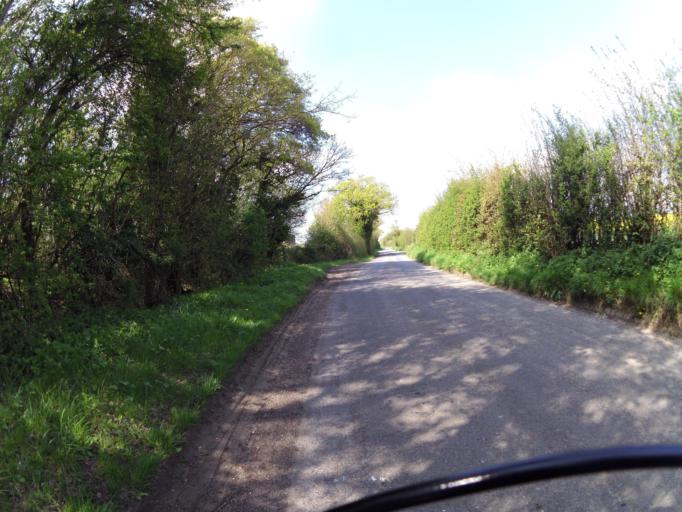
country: GB
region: England
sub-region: Suffolk
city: Bramford
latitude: 52.0821
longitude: 1.0683
